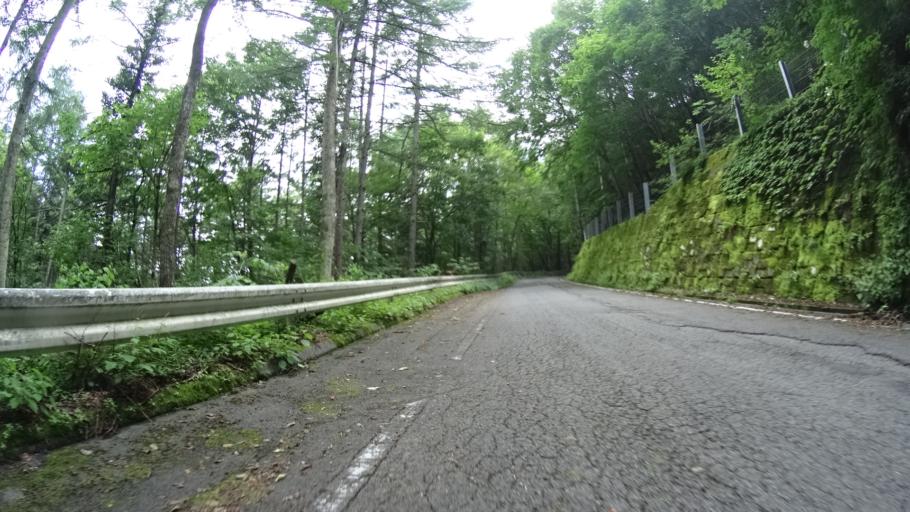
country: JP
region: Nagano
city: Saku
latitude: 36.0725
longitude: 138.6445
